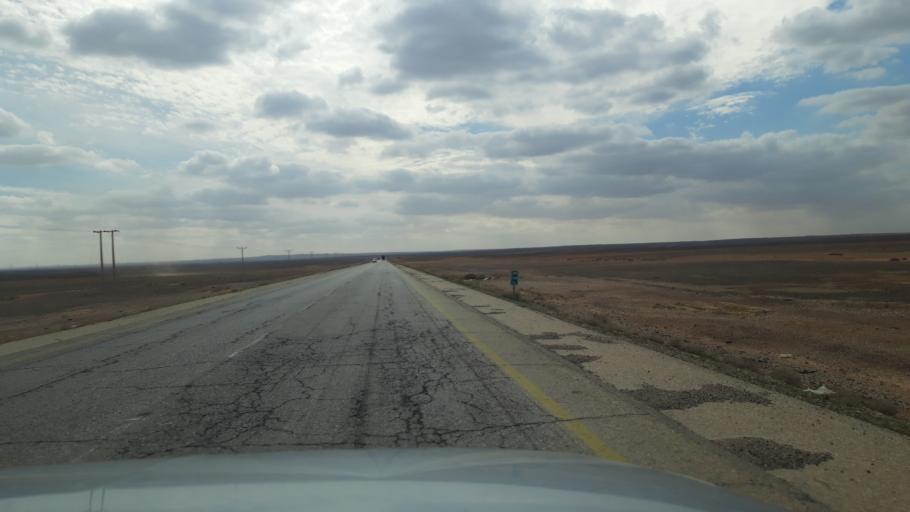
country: JO
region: Amman
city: Al Azraq ash Shamali
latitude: 31.8317
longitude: 36.6257
